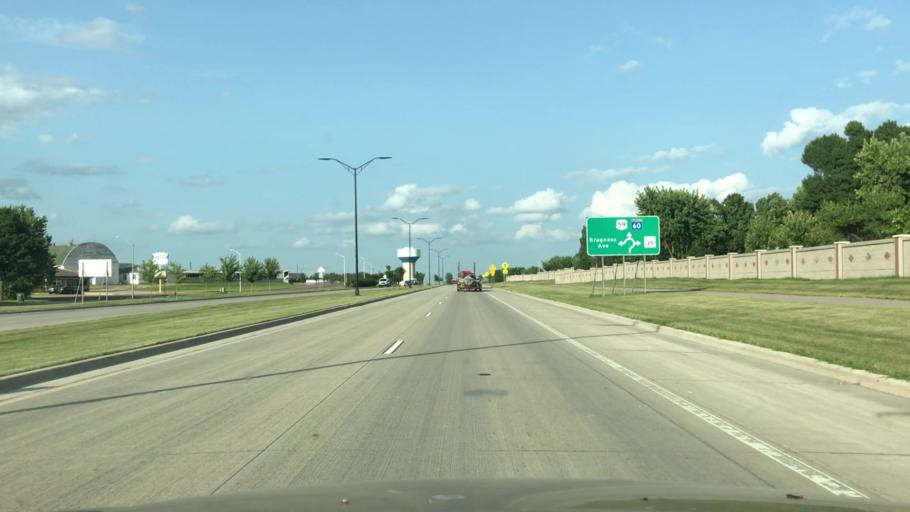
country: US
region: Minnesota
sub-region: Nobles County
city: Worthington
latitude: 43.6181
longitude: -95.5849
